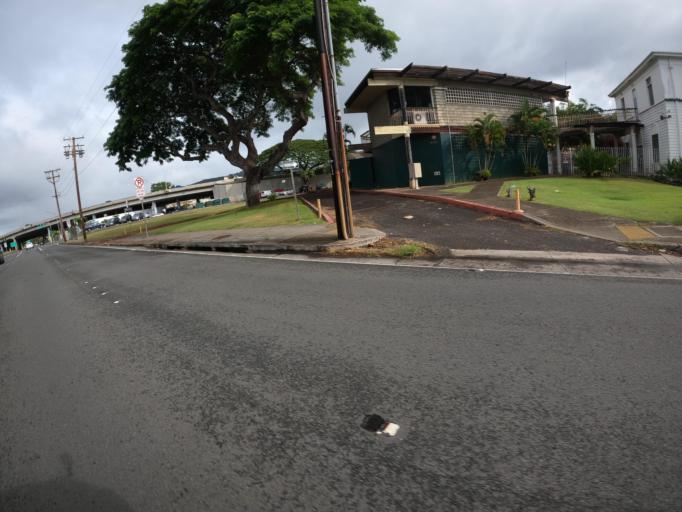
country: US
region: Hawaii
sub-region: Honolulu County
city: Honolulu
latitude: 21.3229
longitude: -157.8643
